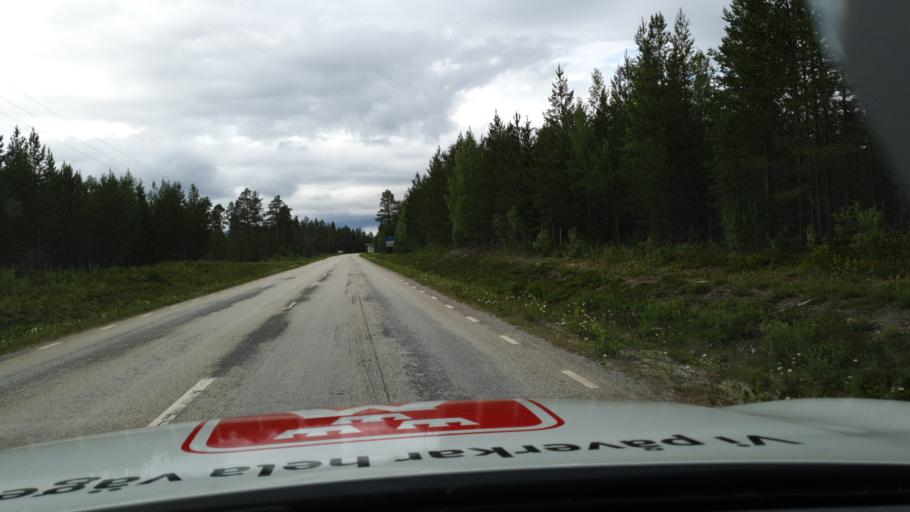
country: SE
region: Jaemtland
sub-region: Bergs Kommun
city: Hoverberg
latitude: 62.5005
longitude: 14.2052
